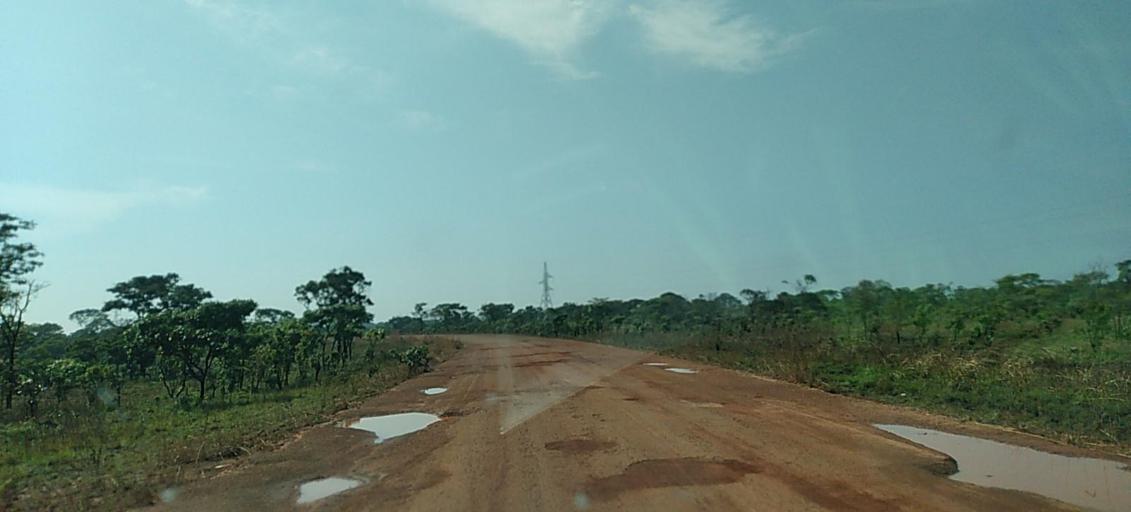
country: ZM
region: North-Western
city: Mwinilunga
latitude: -11.7847
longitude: 25.0261
